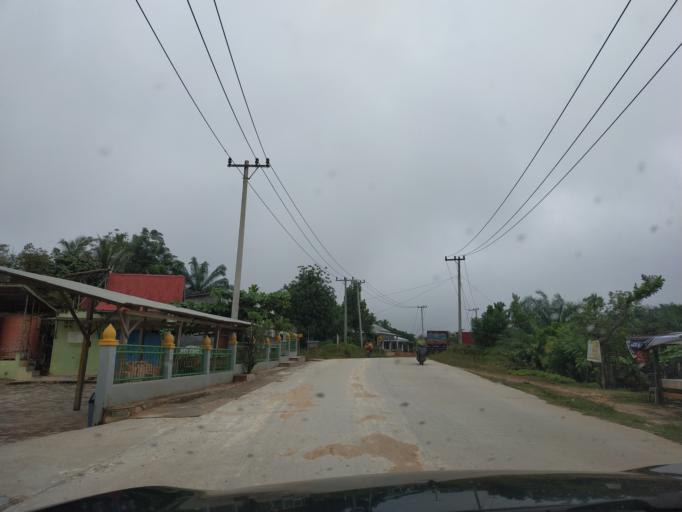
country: ID
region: Riau
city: Pekanbaru
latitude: 0.5047
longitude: 101.5278
